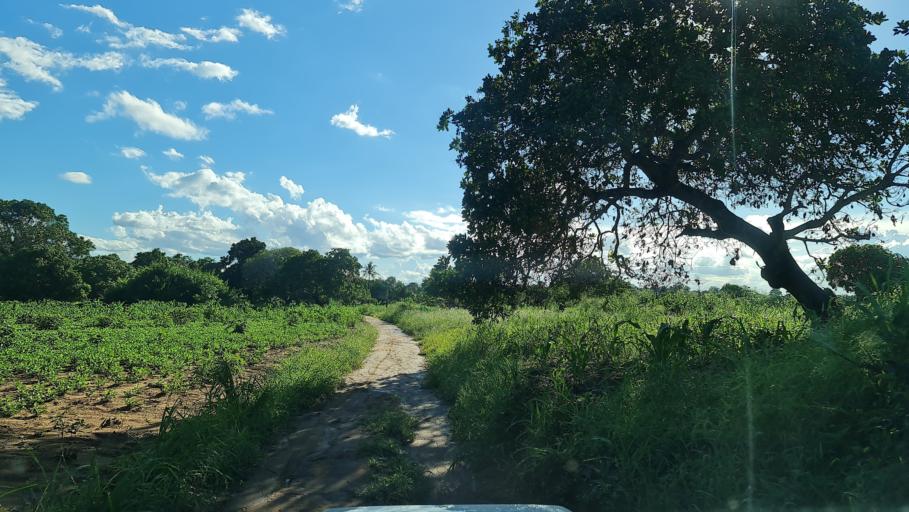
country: MZ
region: Nampula
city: Ilha de Mocambique
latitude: -14.9317
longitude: 40.2154
